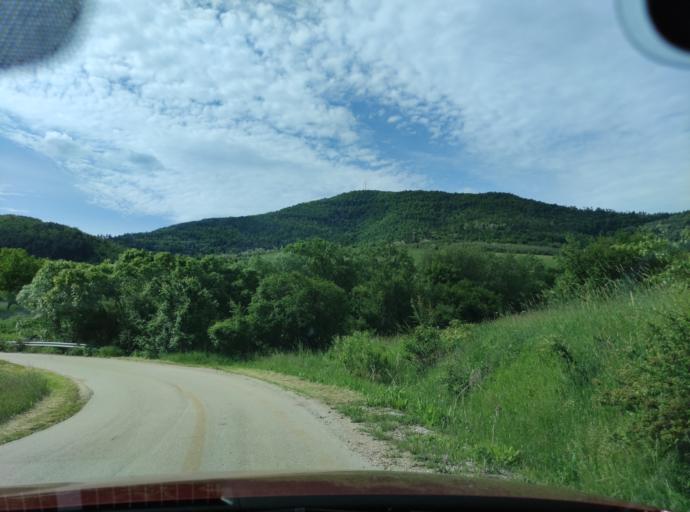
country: BG
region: Vidin
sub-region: Obshtina Belogradchik
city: Belogradchik
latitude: 43.5177
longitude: 22.7280
